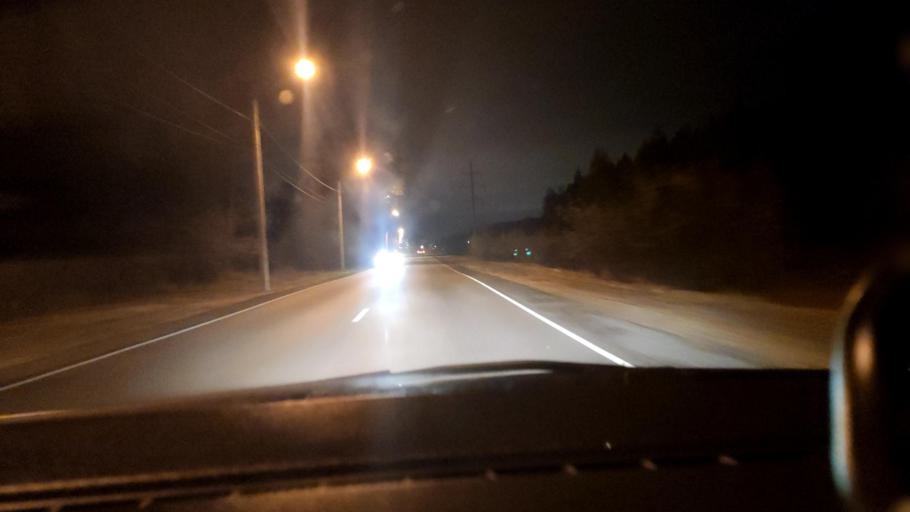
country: RU
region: Voronezj
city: Shilovo
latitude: 51.6107
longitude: 39.0487
